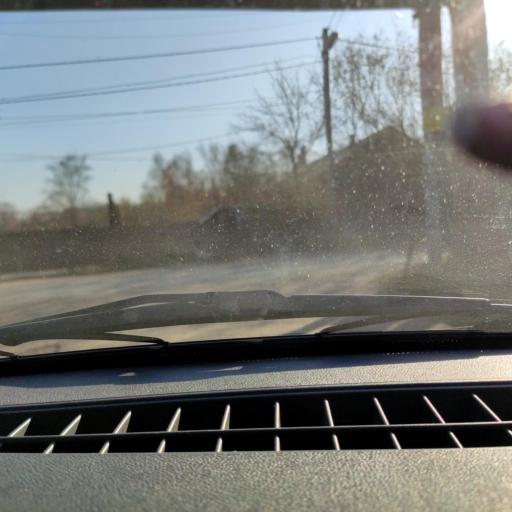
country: RU
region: Bashkortostan
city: Ufa
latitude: 54.7991
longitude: 56.1525
